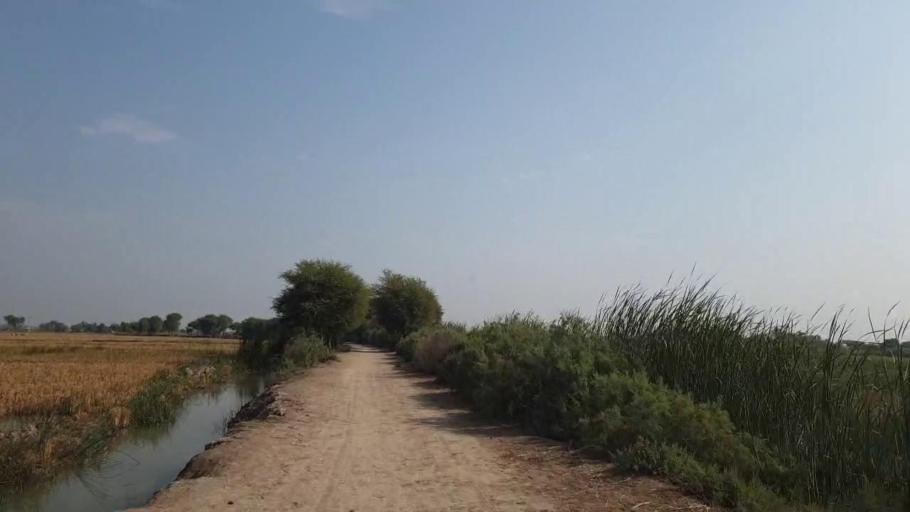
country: PK
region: Sindh
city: Tando Muhammad Khan
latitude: 25.0666
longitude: 68.4371
